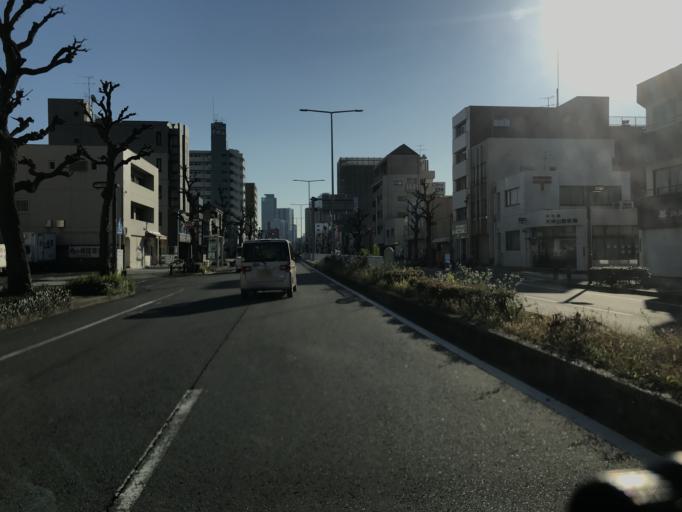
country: JP
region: Aichi
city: Nagoya-shi
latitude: 35.1918
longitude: 136.8872
